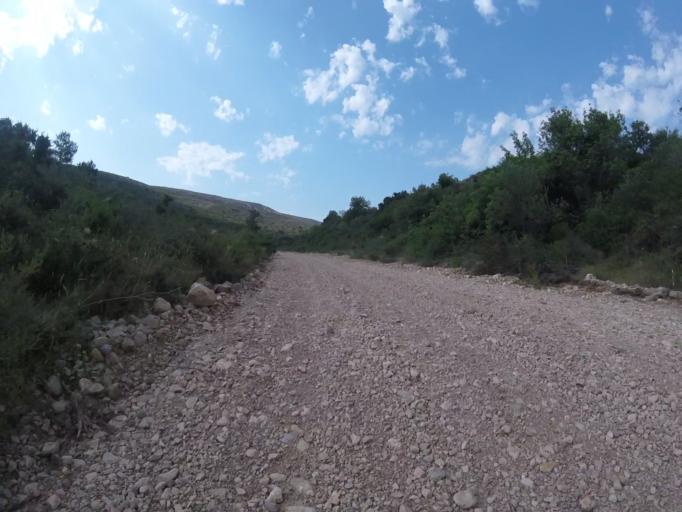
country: ES
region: Valencia
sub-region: Provincia de Castello
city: Alcala de Xivert
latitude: 40.3316
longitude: 0.1935
